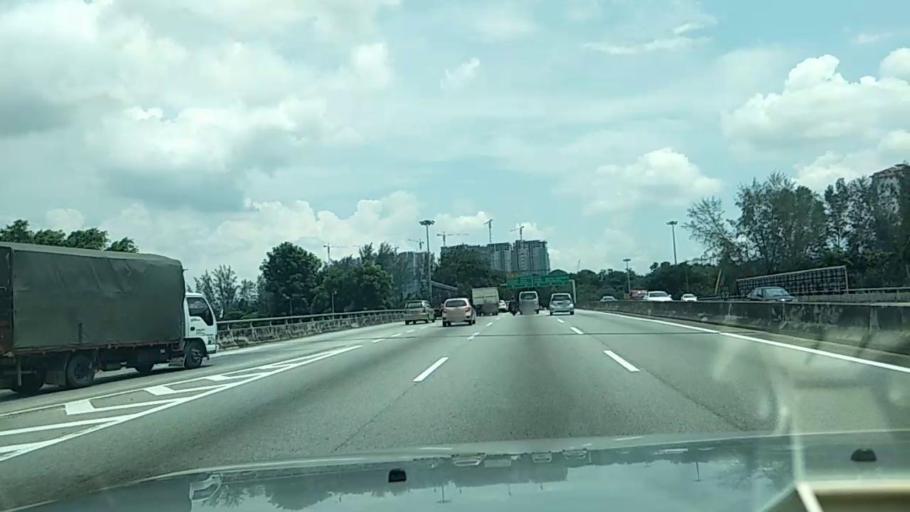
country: MY
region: Selangor
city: Kampong Baharu Balakong
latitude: 3.0642
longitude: 101.7041
